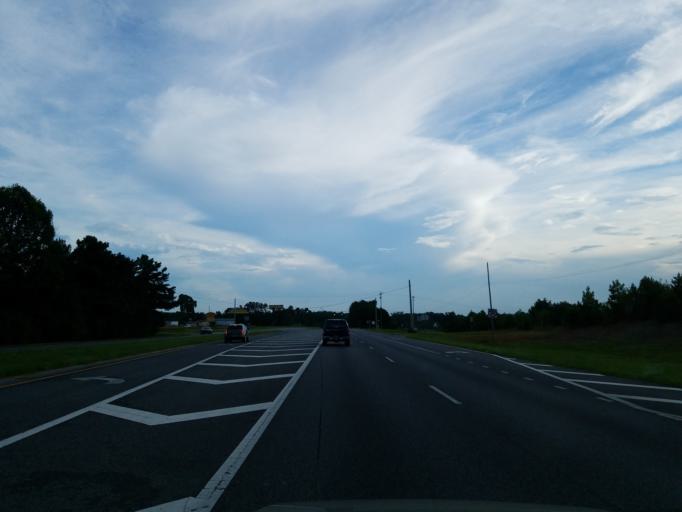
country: US
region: Georgia
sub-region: Dawson County
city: Dawsonville
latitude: 34.3136
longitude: -84.0649
